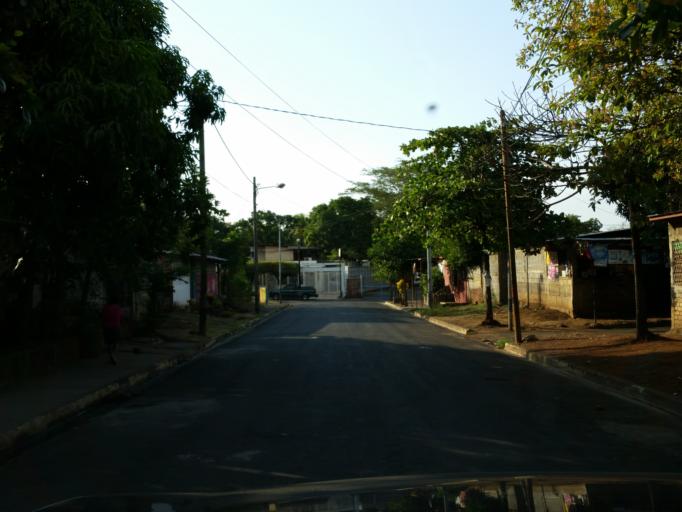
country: NI
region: Managua
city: Managua
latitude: 12.1194
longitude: -86.2715
